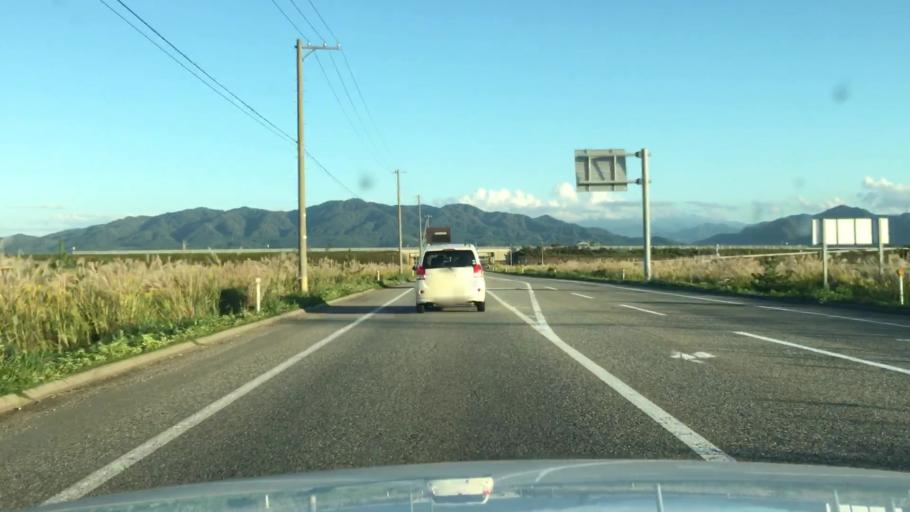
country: JP
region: Niigata
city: Murakami
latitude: 38.1206
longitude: 139.4089
